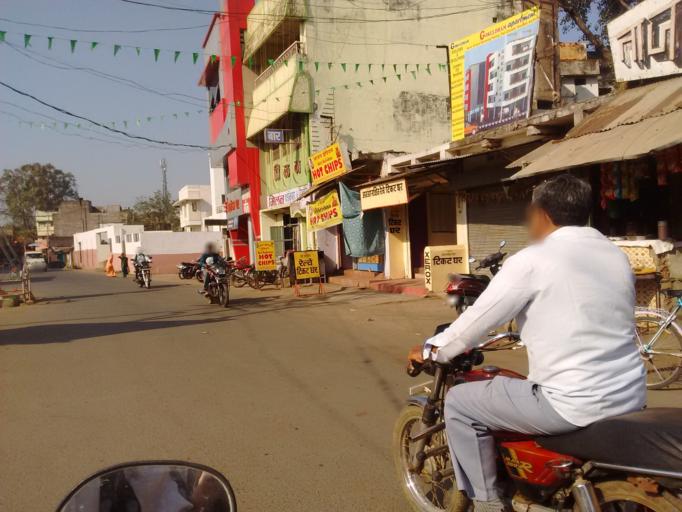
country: IN
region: Maharashtra
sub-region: Gondiya
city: Gondia
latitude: 21.4631
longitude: 80.1900
